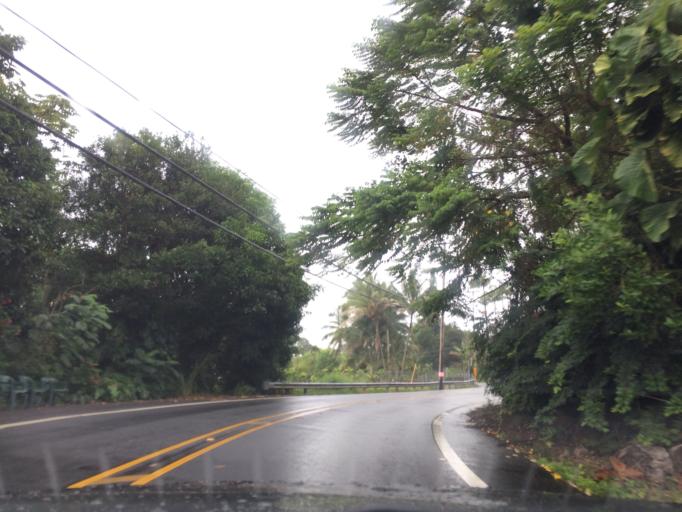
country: US
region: Hawaii
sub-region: Hawaii County
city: Hilo
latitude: 19.6945
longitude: -155.1208
